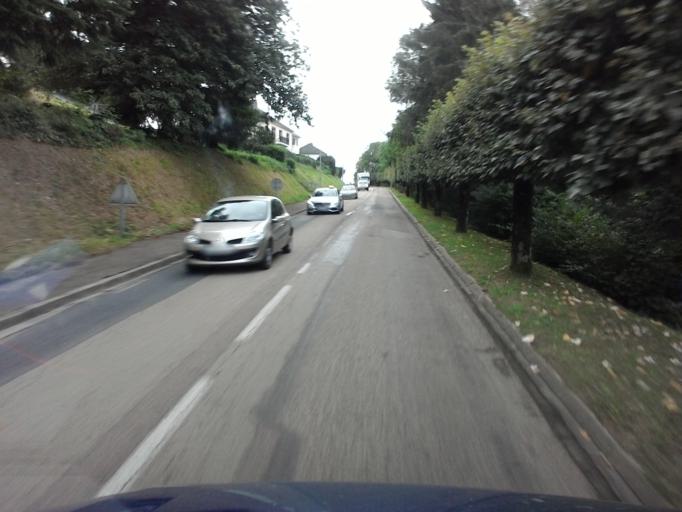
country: FR
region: Bourgogne
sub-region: Departement de la Nievre
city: Chateau-Chinon(Ville)
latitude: 47.0763
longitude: 3.9277
